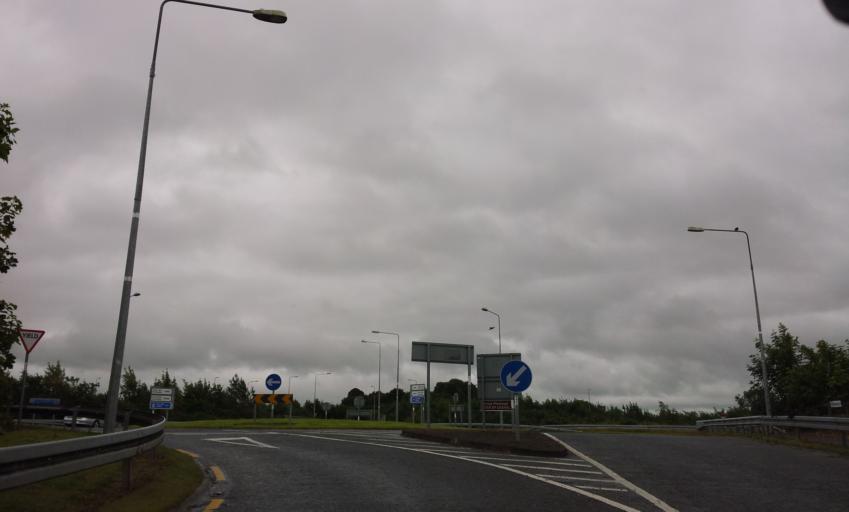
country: IE
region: Munster
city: Cashel
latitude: 52.5095
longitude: -7.8728
